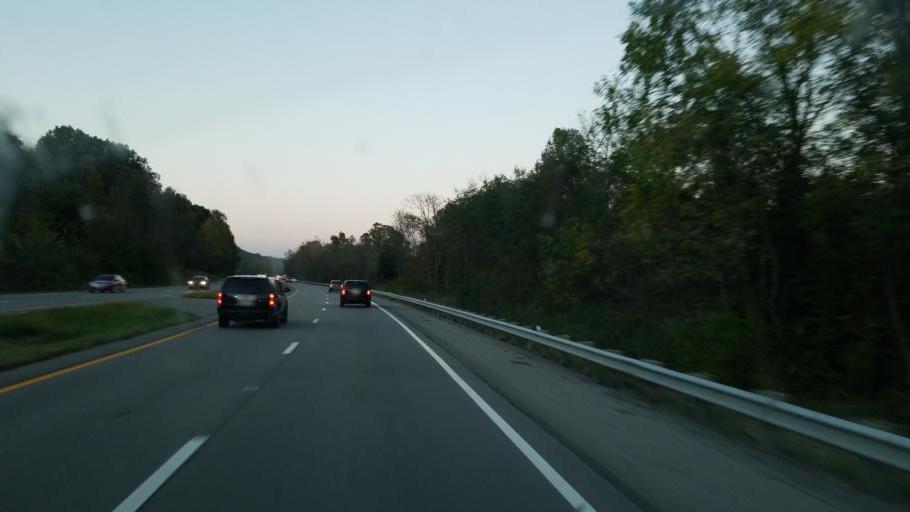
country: US
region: Ohio
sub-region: Ross County
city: Chillicothe
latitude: 39.2613
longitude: -82.9696
